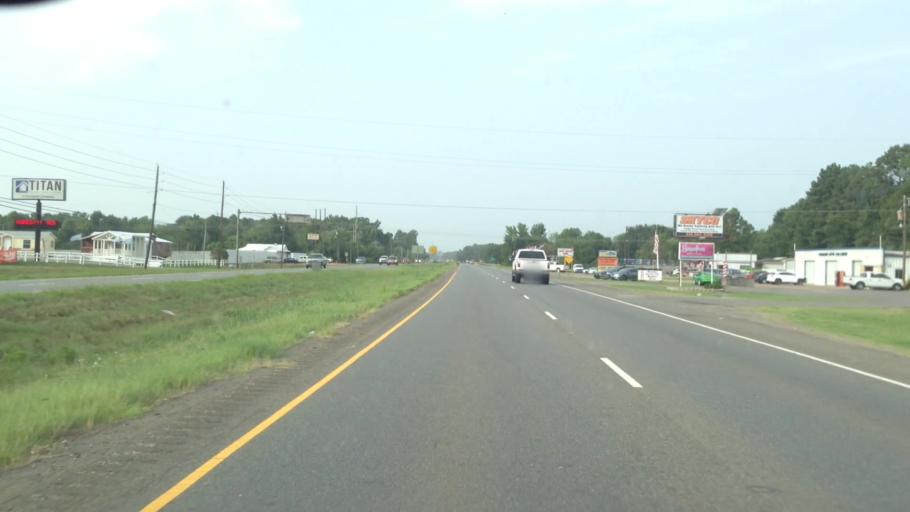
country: US
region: Louisiana
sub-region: De Soto Parish
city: Stonewall
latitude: 32.3802
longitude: -93.8201
